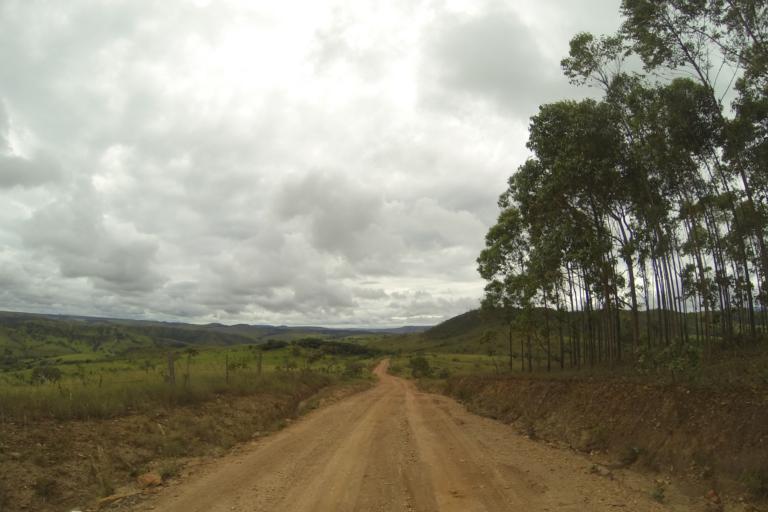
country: BR
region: Minas Gerais
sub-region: Ibia
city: Ibia
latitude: -19.7509
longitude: -46.4960
